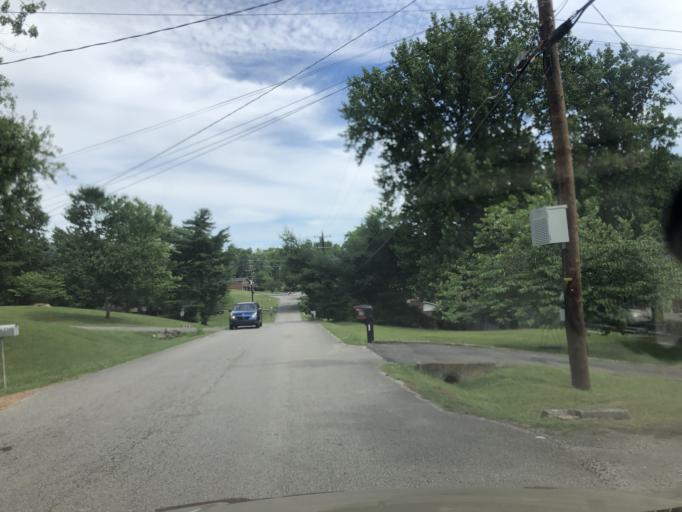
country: US
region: Tennessee
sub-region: Davidson County
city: Lakewood
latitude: 36.2596
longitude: -86.6213
